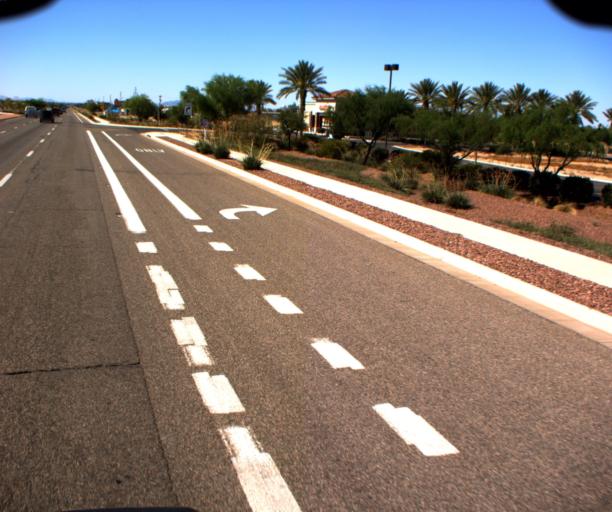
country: US
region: Arizona
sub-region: Pinal County
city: Casa Grande
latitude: 32.9372
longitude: -111.7570
